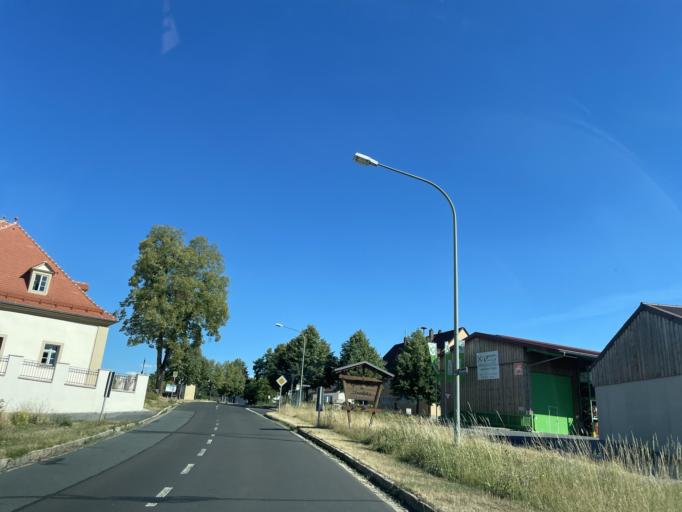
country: DE
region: Bavaria
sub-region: Upper Palatinate
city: Trabitz
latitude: 49.8014
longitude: 11.8954
